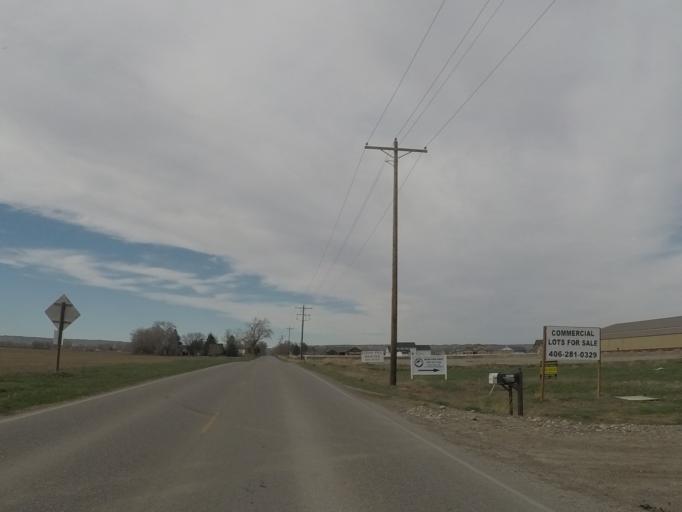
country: US
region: Montana
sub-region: Yellowstone County
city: Laurel
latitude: 45.7199
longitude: -108.6587
